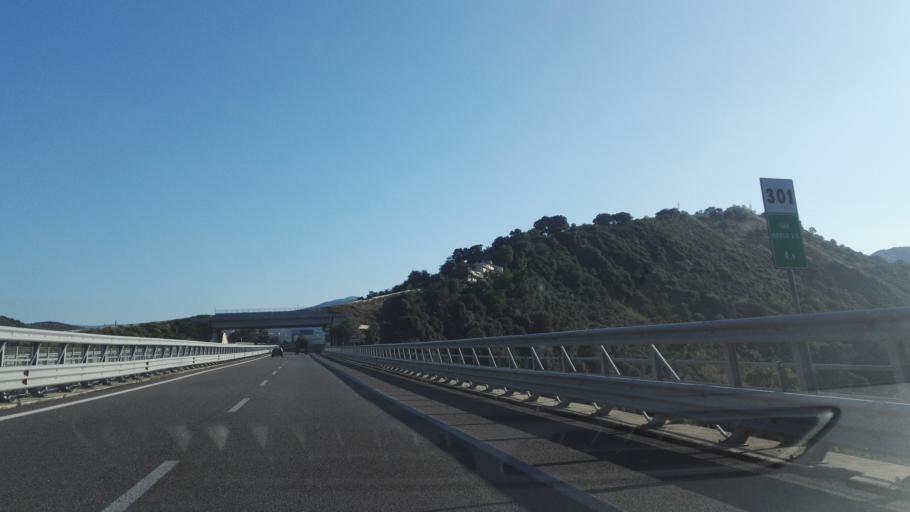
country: IT
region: Calabria
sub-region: Provincia di Catanzaro
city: Nocera Scalo
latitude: 39.0351
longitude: 16.1355
